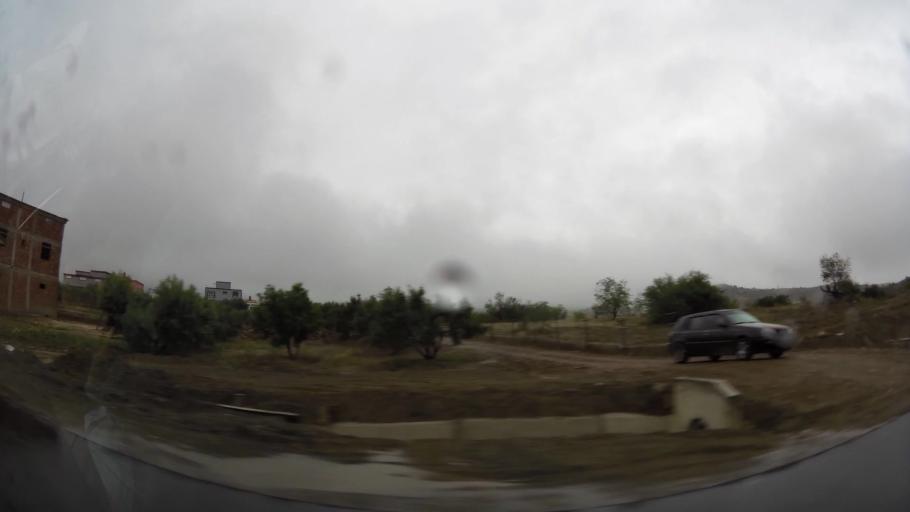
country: MA
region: Taza-Al Hoceima-Taounate
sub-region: Taza
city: Aknoul
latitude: 34.8238
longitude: -3.7235
